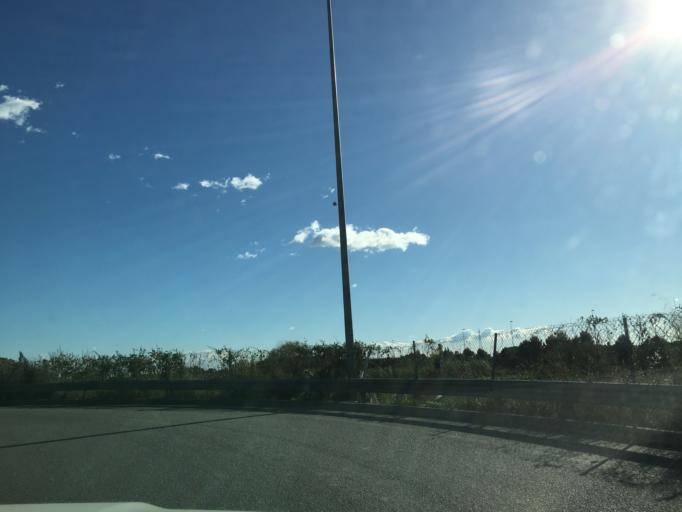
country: ES
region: Catalonia
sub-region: Provincia de Barcelona
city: Sant Feliu de Llobregat
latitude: 41.3677
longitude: 2.0495
